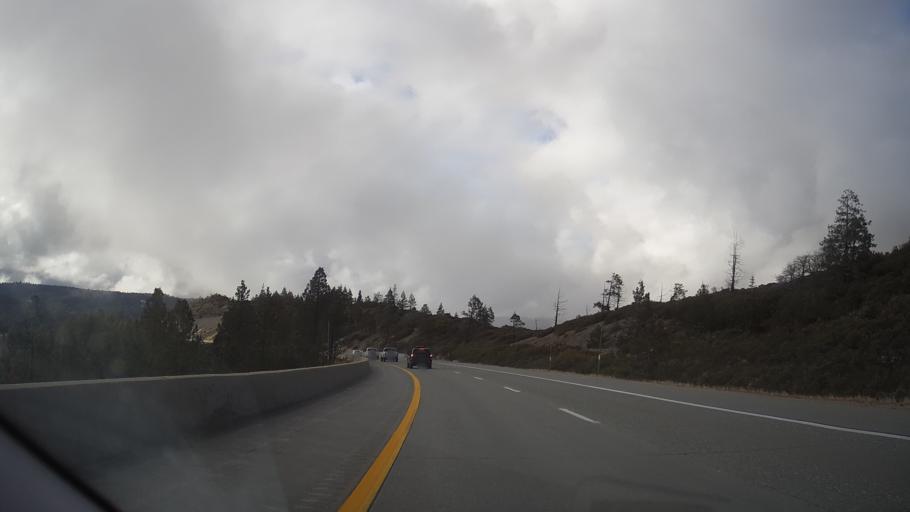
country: US
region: California
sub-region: Sierra County
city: Downieville
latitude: 39.3106
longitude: -120.6373
